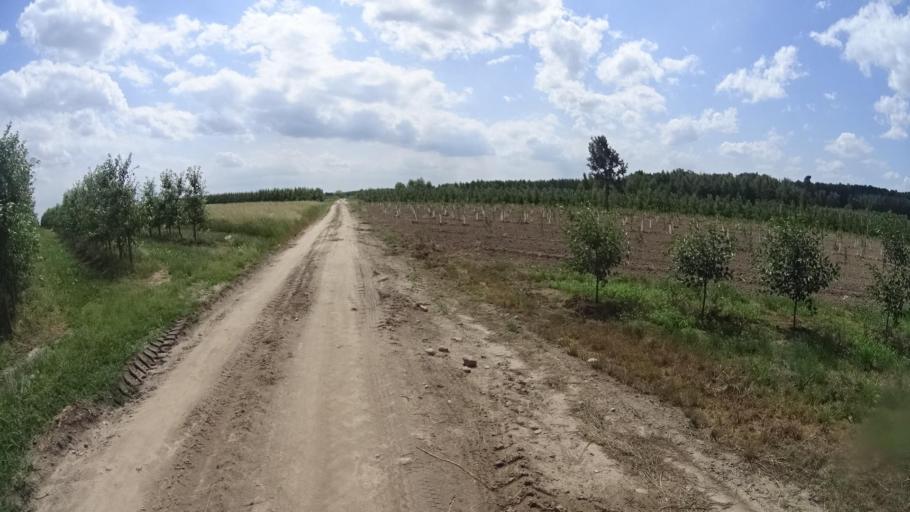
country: PL
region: Masovian Voivodeship
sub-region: Powiat grojecki
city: Goszczyn
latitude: 51.7069
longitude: 20.8286
